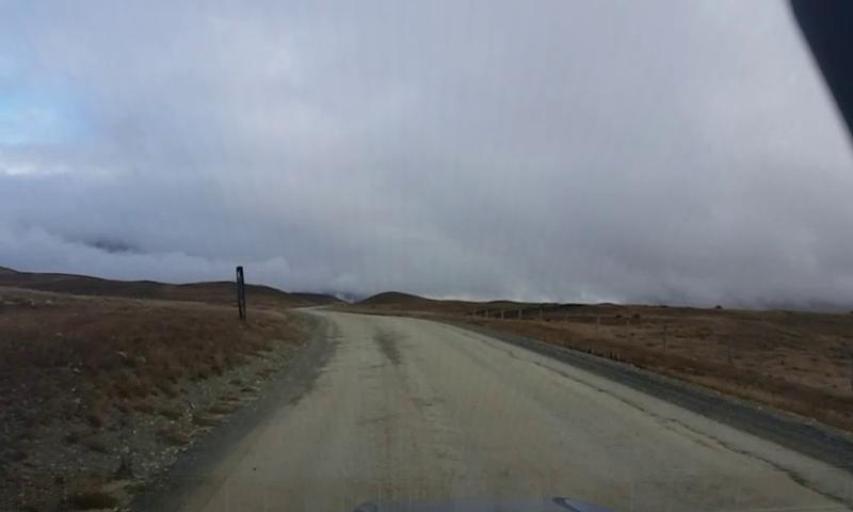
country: NZ
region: Canterbury
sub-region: Ashburton District
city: Methven
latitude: -43.6143
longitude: 171.1510
